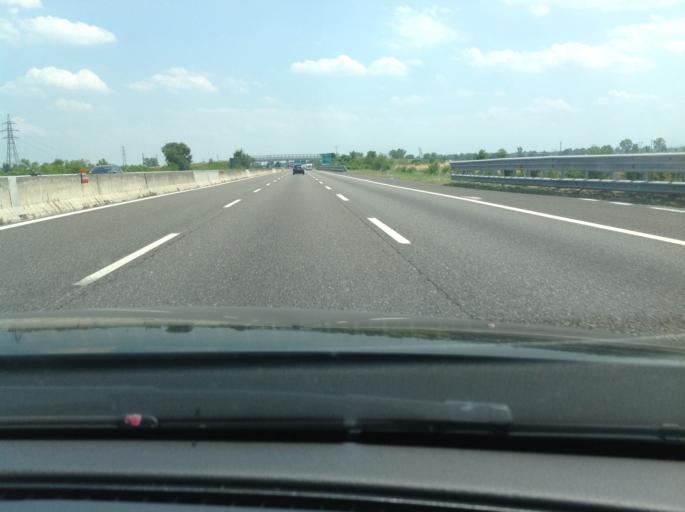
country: IT
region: Emilia-Romagna
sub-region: Provincia di Piacenza
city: Roveleto
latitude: 44.9705
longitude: 9.8869
